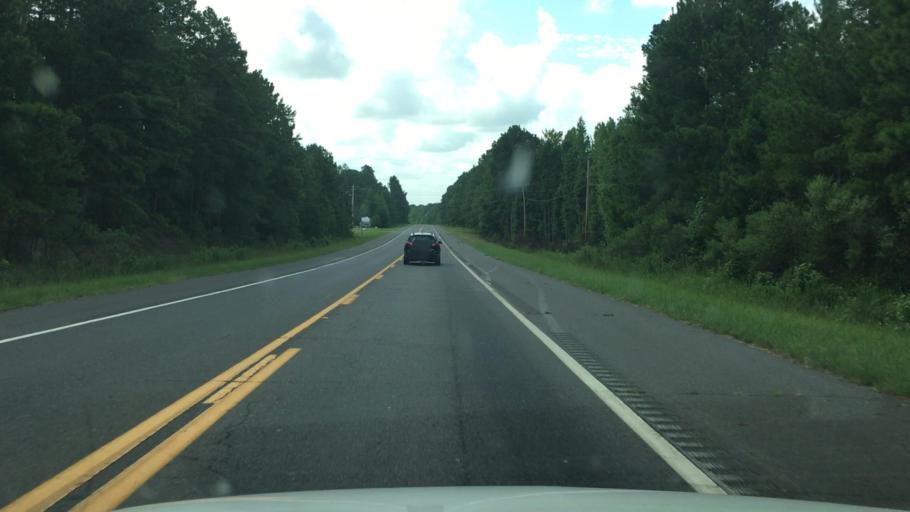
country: US
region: Arkansas
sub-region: Clark County
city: Arkadelphia
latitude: 34.2080
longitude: -93.0794
